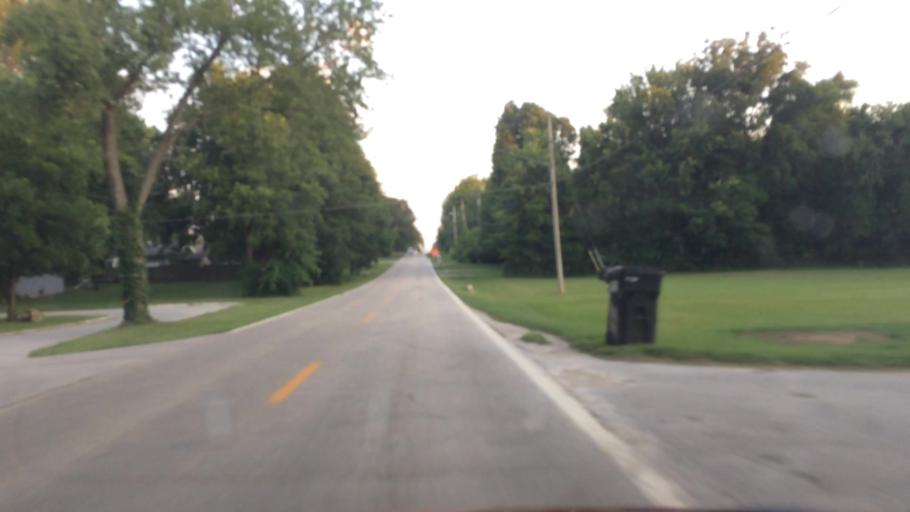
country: US
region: Missouri
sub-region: Greene County
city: Springfield
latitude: 37.2106
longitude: -93.3740
